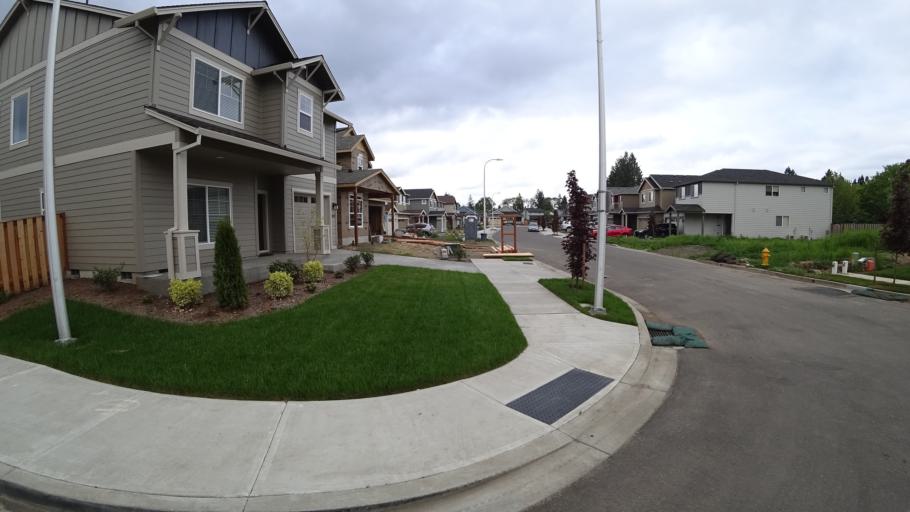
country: US
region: Oregon
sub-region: Washington County
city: Hillsboro
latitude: 45.5339
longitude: -122.9905
